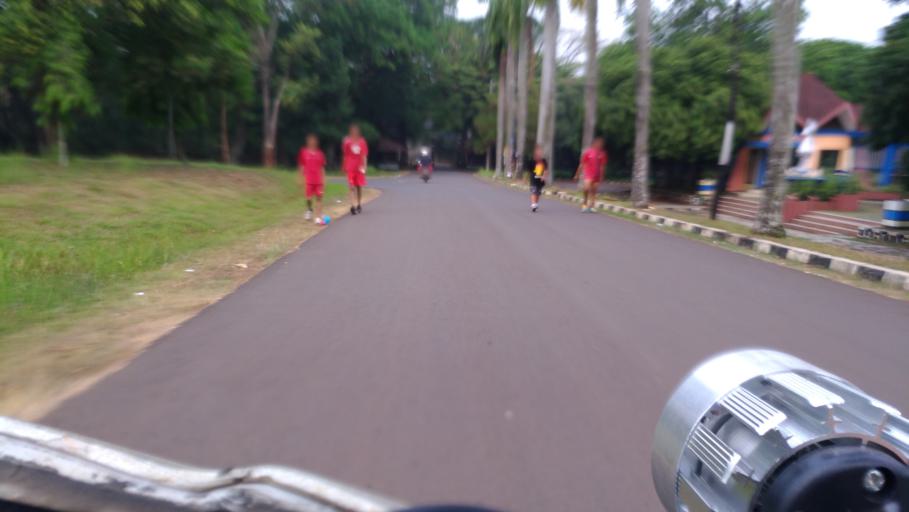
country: ID
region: West Java
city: Cileungsir
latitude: -6.3646
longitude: 106.8964
